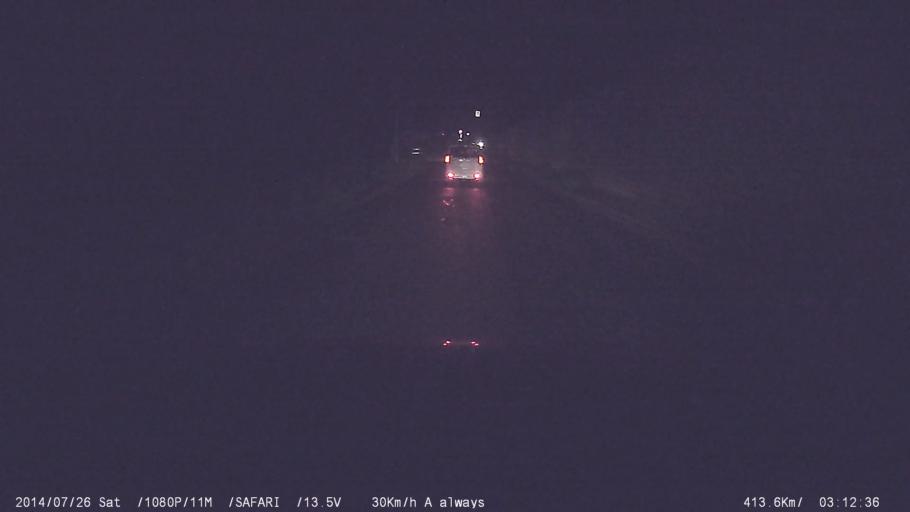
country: IN
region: Kerala
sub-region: Palakkad district
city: Palakkad
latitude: 10.6643
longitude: 76.5727
